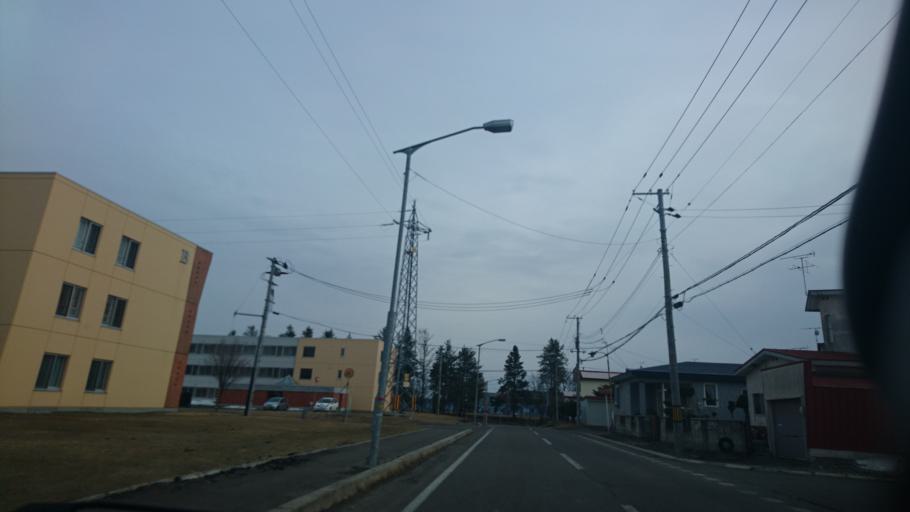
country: JP
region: Hokkaido
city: Otofuke
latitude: 42.9976
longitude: 143.1934
